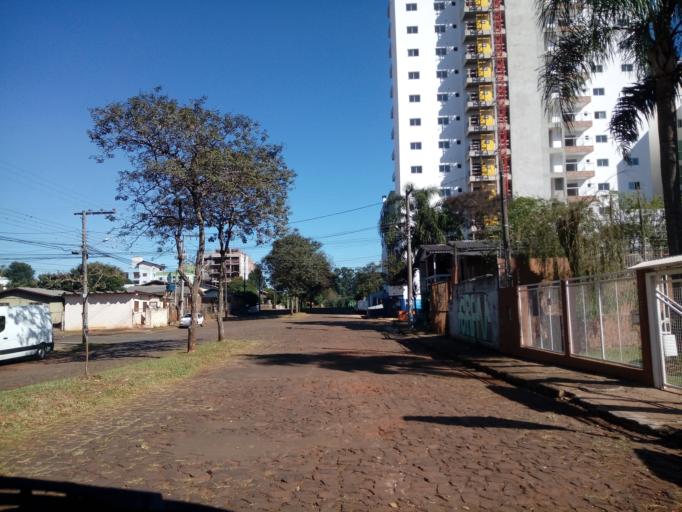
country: BR
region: Santa Catarina
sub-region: Chapeco
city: Chapeco
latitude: -27.1009
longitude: -52.6239
